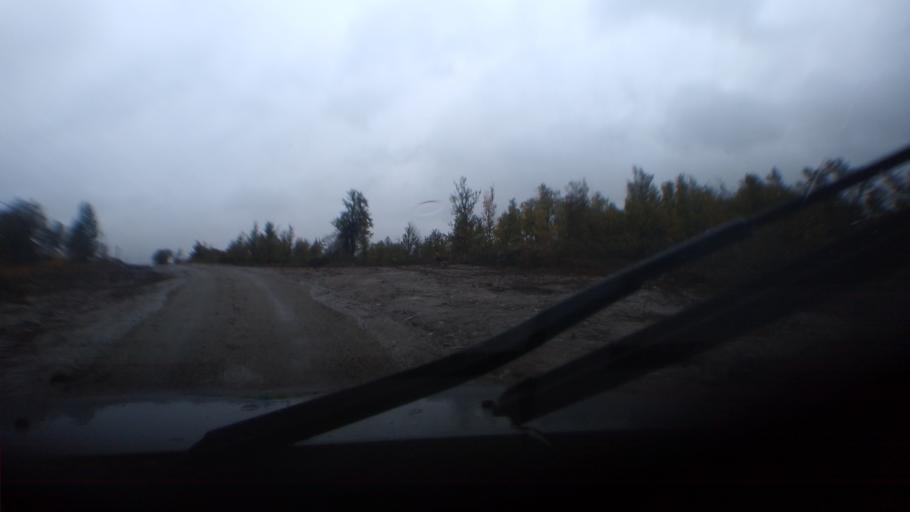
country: NO
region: Oppland
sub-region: Ringebu
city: Ringebu
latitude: 61.6599
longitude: 10.1042
